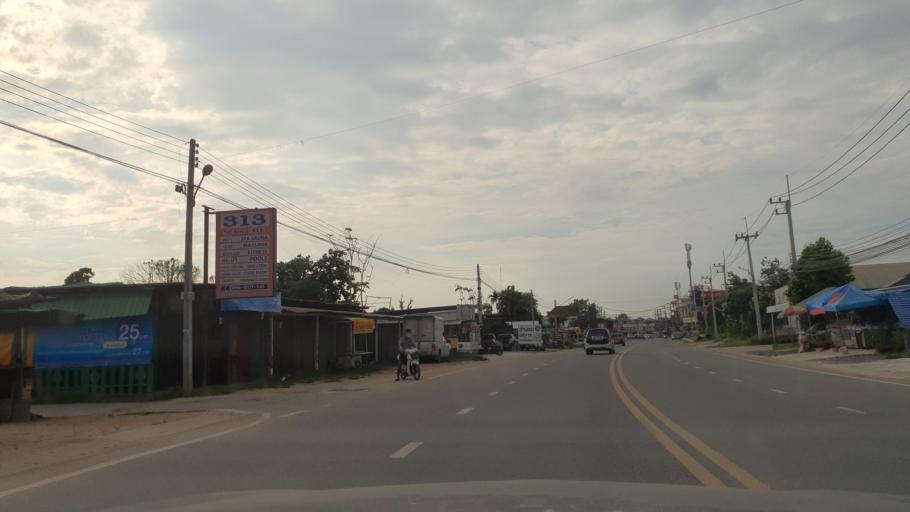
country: TH
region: Chon Buri
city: Phatthaya
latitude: 12.9432
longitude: 100.9420
